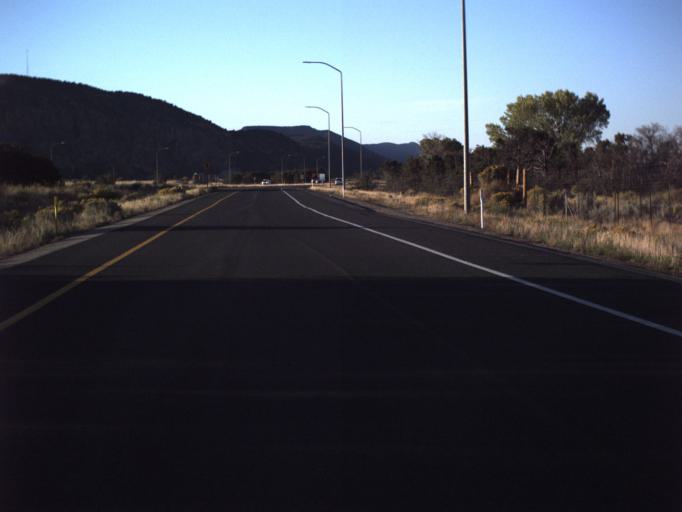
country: US
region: Utah
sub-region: Iron County
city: Cedar City
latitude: 37.5145
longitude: -113.2126
